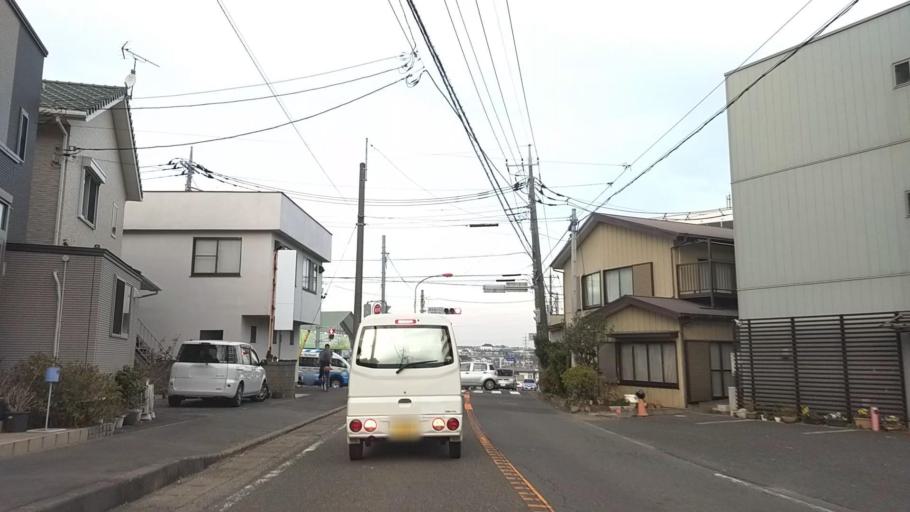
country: JP
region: Kanagawa
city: Atsugi
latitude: 35.4357
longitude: 139.3380
